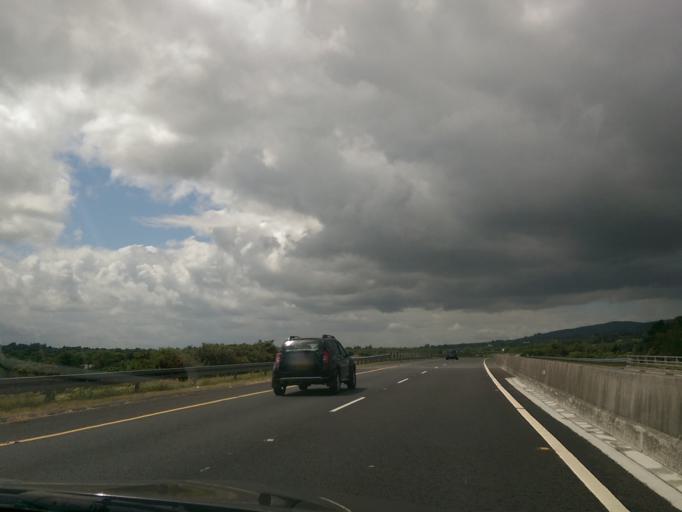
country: IE
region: Munster
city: Tipperary
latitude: 52.3178
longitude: -8.1109
